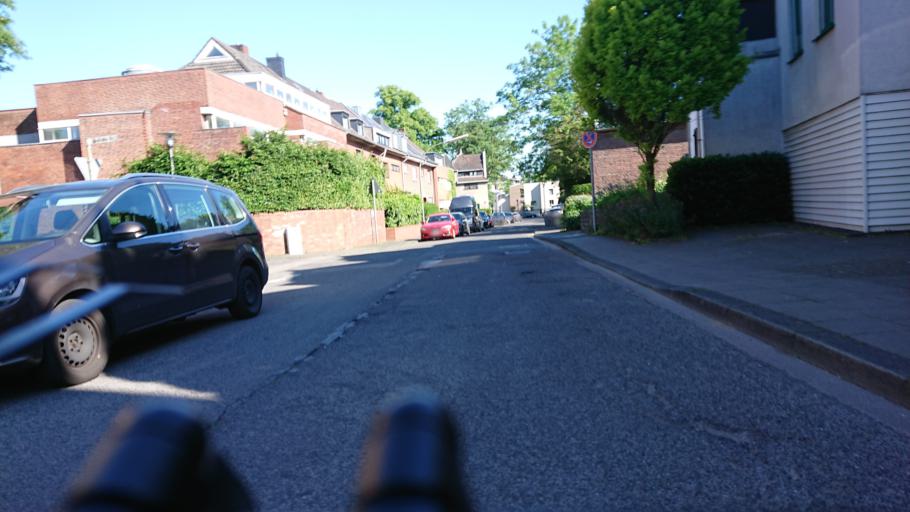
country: DE
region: North Rhine-Westphalia
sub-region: Regierungsbezirk Koln
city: Mengenich
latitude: 50.9429
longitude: 6.8745
